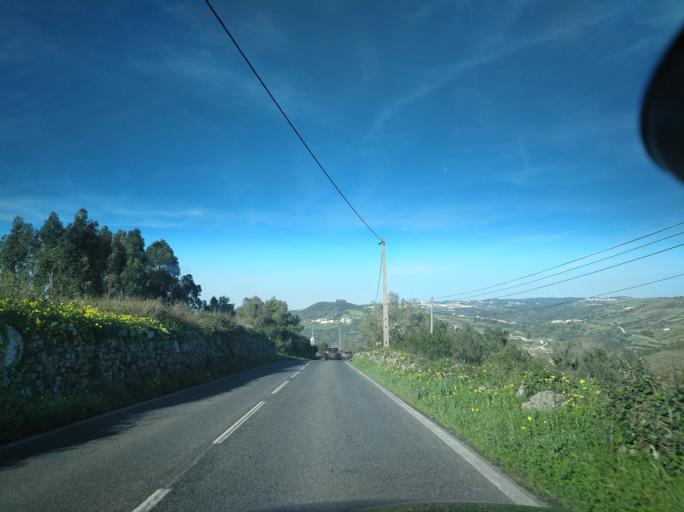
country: PT
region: Lisbon
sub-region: Sintra
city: Pero Pinheiro
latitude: 38.8789
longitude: -9.3298
